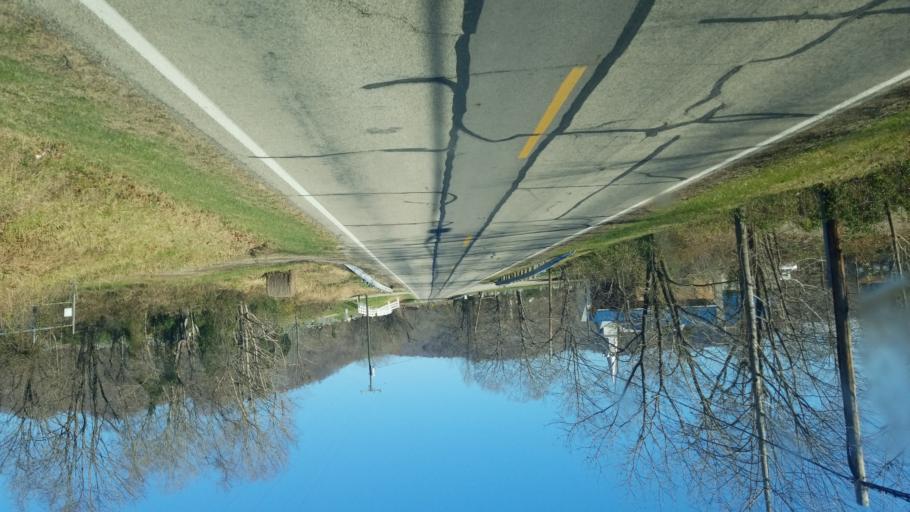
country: US
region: Kentucky
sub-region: Lewis County
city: Vanceburg
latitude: 38.6353
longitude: -83.2177
